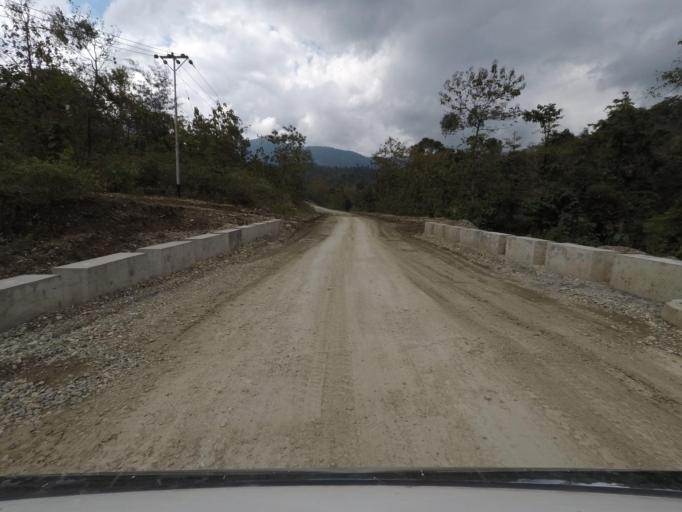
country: TL
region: Viqueque
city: Viqueque
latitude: -8.8165
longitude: 126.3802
